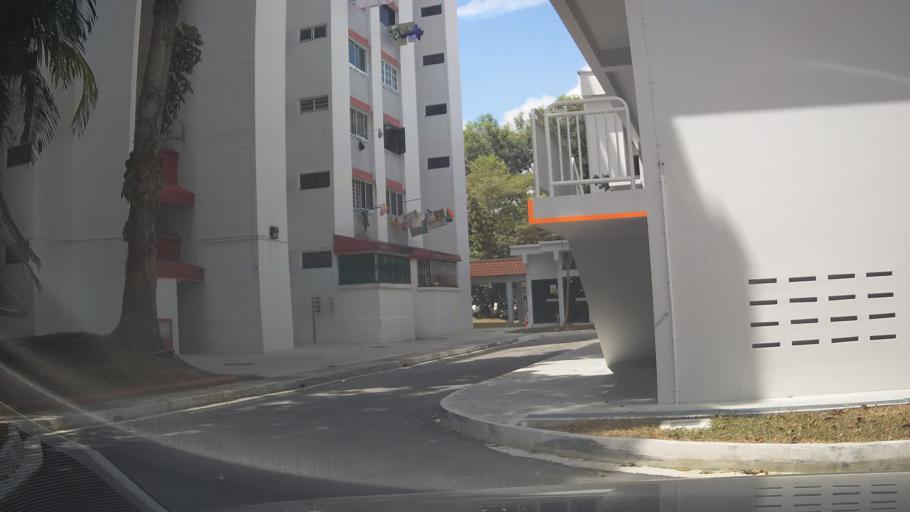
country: SG
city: Singapore
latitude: 1.3573
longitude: 103.9448
